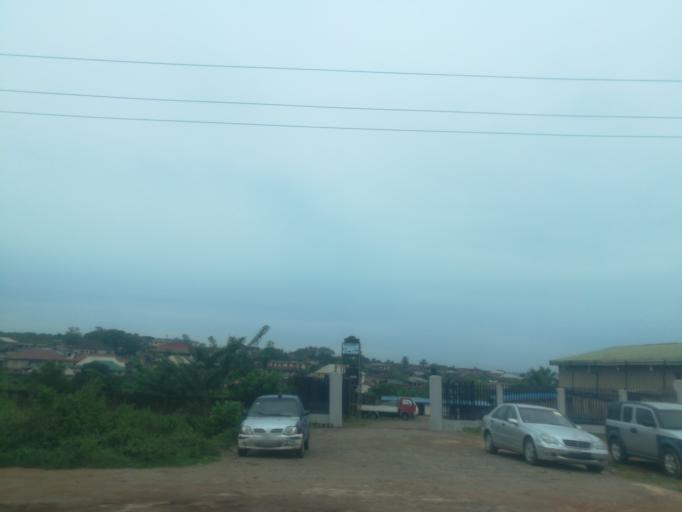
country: NG
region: Oyo
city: Egbeda
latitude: 7.3815
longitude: 3.9959
